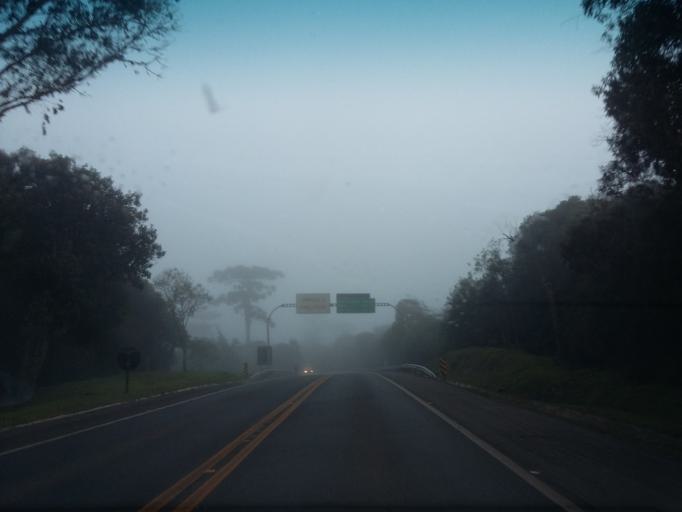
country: BR
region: Santa Catarina
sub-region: Curitibanos
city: Curitibanos
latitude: -27.2983
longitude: -50.4275
